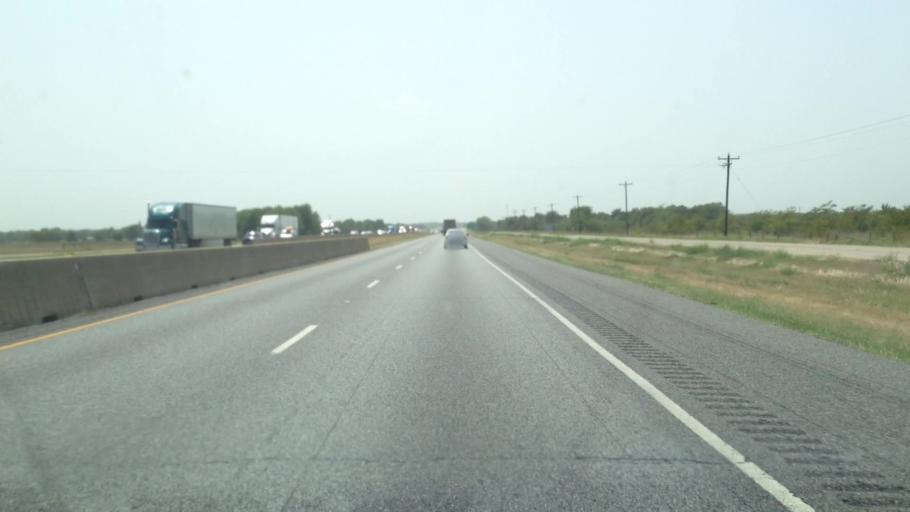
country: US
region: Texas
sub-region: Hunt County
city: Commerce
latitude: 33.1316
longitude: -95.9180
